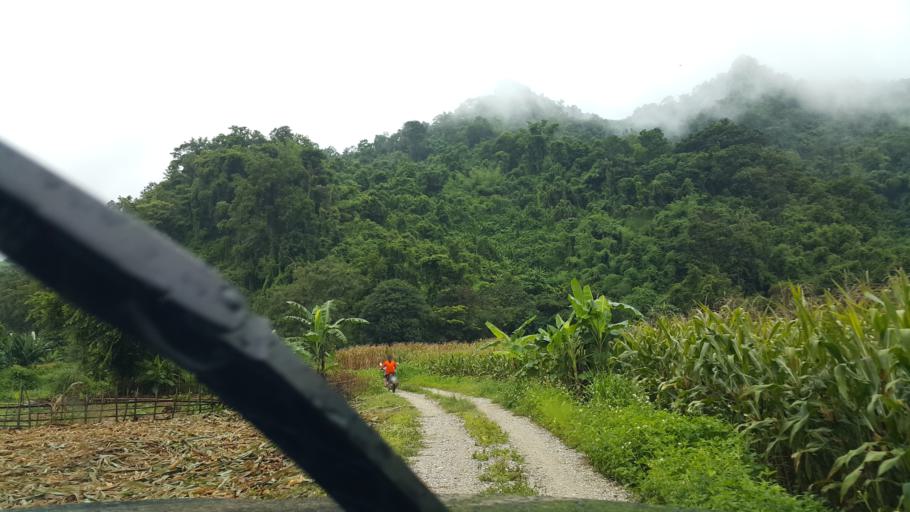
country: TH
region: Phayao
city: Chiang Kham
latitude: 19.5006
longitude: 100.4547
